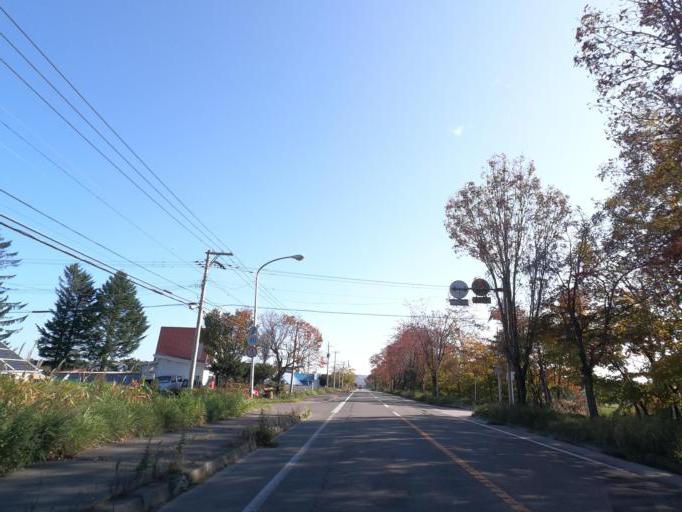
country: JP
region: Hokkaido
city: Obihiro
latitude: 42.9445
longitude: 143.2362
